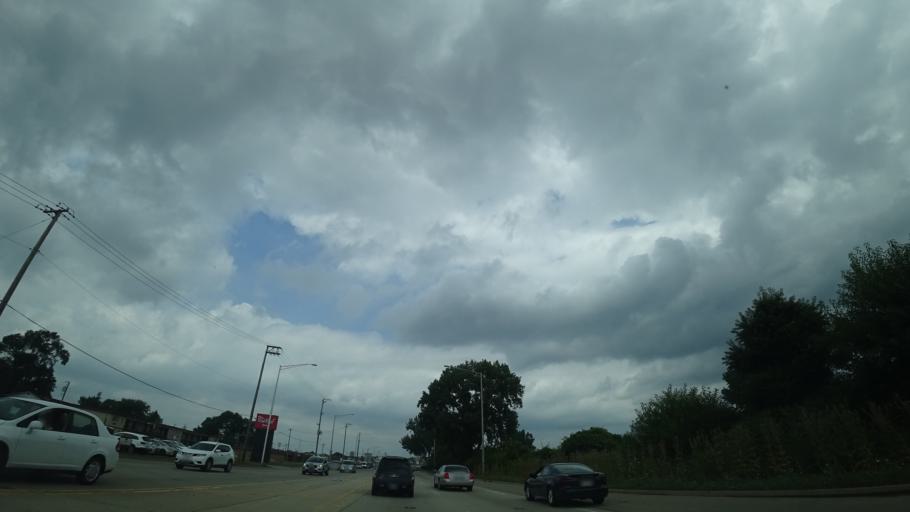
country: US
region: Illinois
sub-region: Cook County
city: Alsip
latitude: 41.6666
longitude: -87.7388
